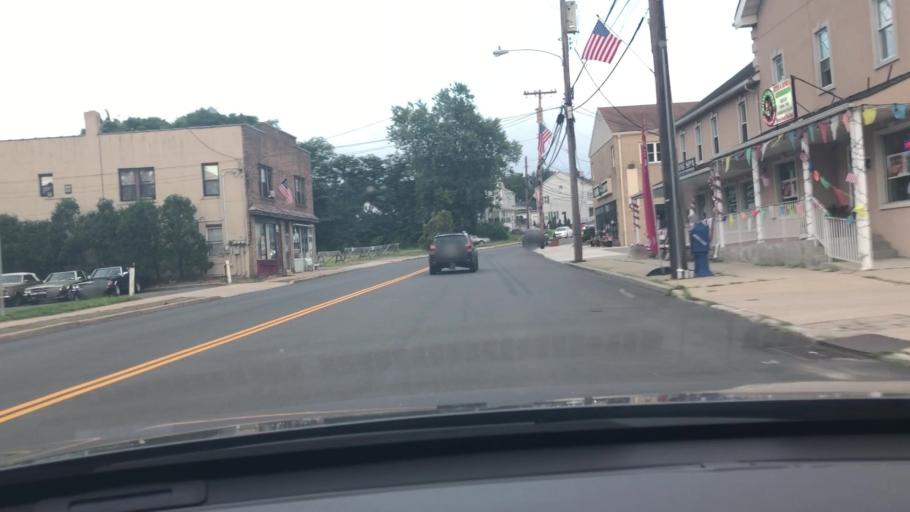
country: US
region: New Jersey
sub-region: Middlesex County
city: Milltown
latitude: 40.4505
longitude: -74.4359
